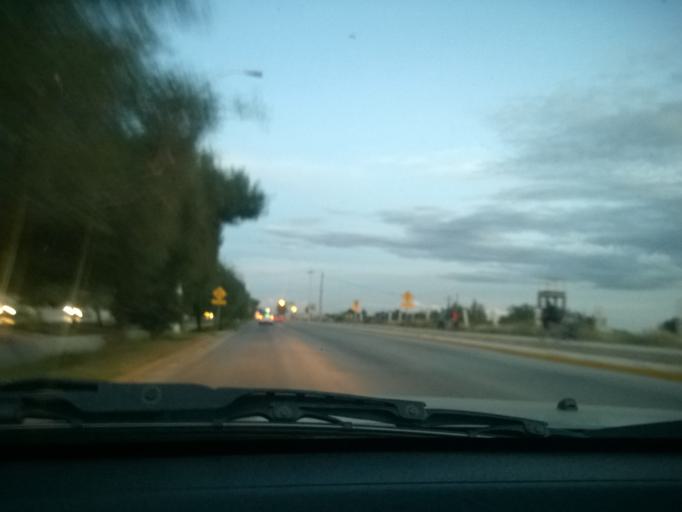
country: MX
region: Guanajuato
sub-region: Leon
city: San Jose de Duran (Los Troncoso)
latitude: 21.0707
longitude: -101.6425
